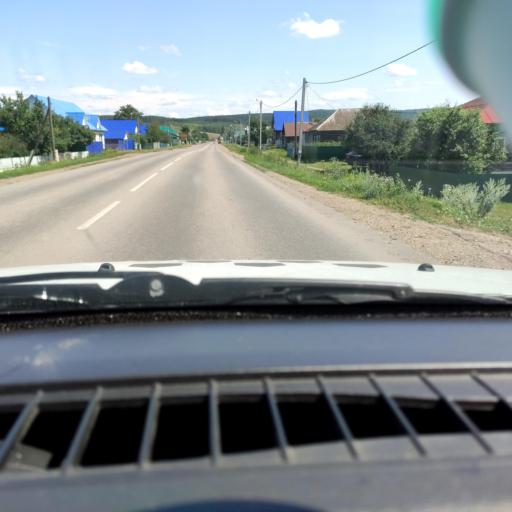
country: RU
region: Bashkortostan
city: Mesyagutovo
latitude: 55.5296
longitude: 58.2624
